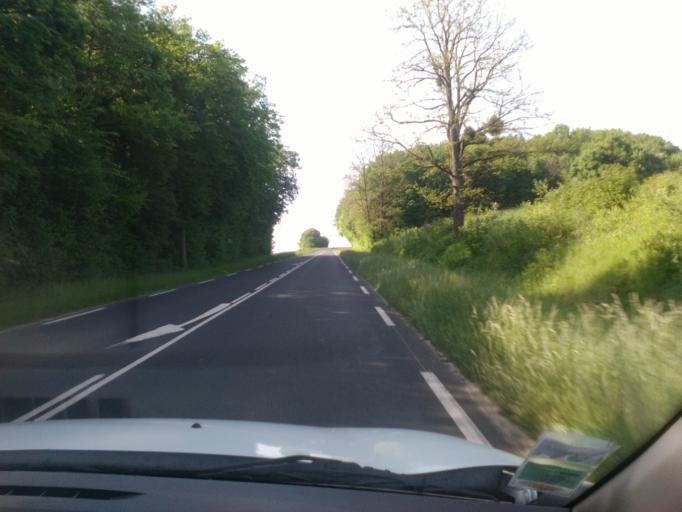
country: FR
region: Lorraine
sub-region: Departement des Vosges
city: Mirecourt
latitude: 48.3388
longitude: 6.1399
